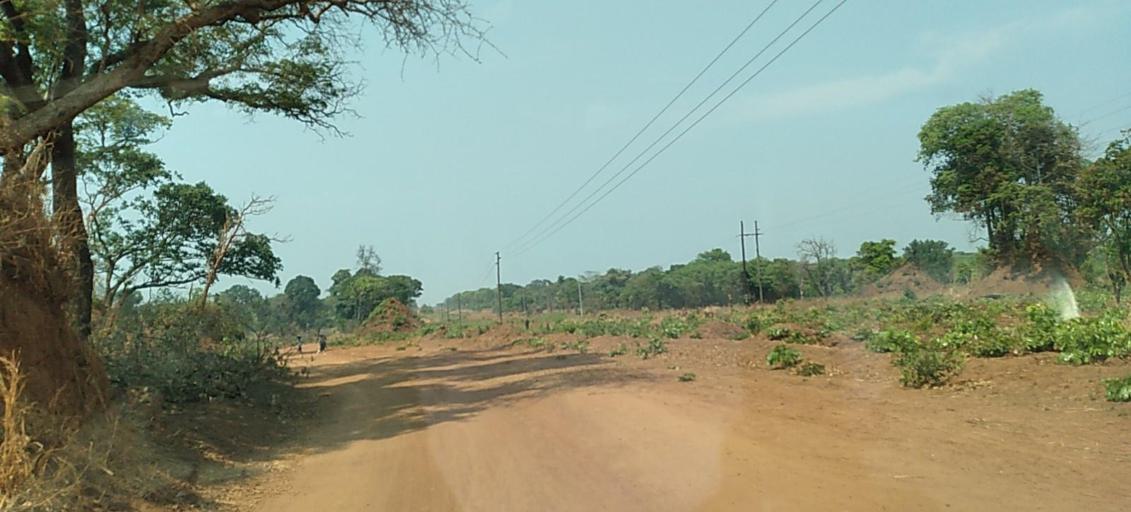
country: ZM
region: Copperbelt
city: Chingola
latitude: -13.0475
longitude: 27.4318
